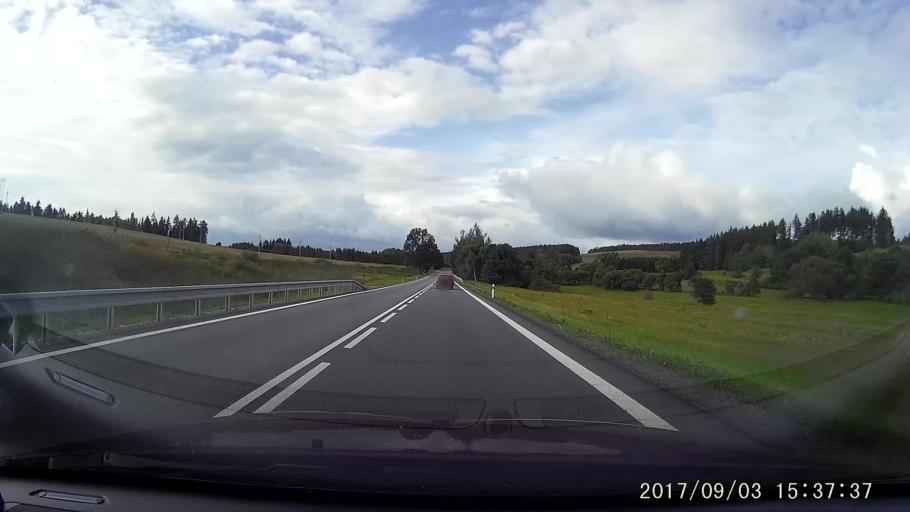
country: CZ
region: Vysocina
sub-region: Okres Jihlava
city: Jihlava
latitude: 49.3074
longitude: 15.5765
